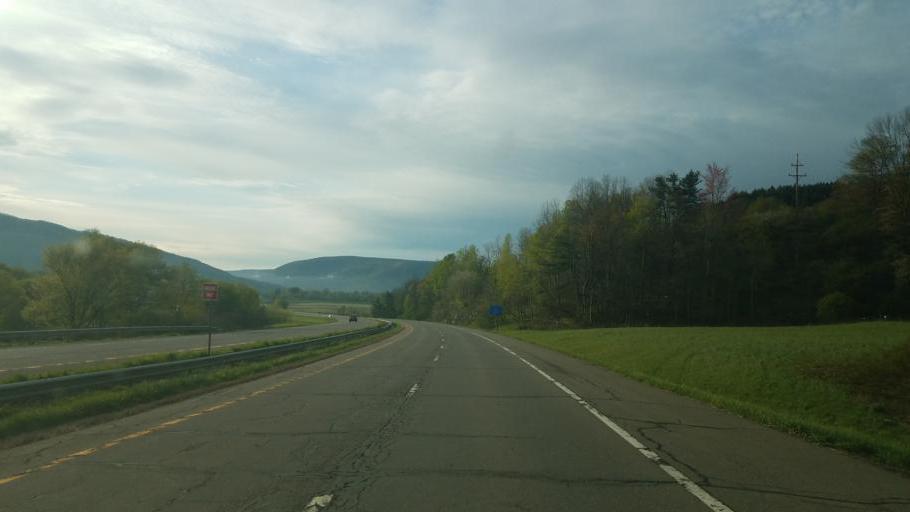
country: US
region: New York
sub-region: Steuben County
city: Canisteo
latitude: 42.2836
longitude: -77.6264
